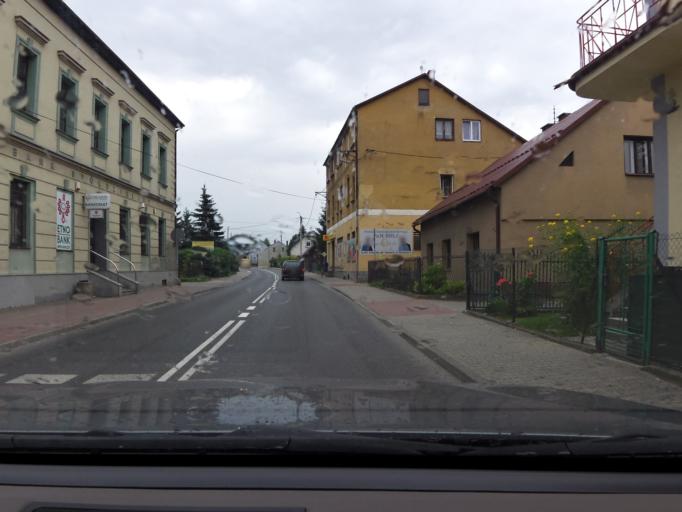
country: PL
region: Silesian Voivodeship
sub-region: Powiat zywiecki
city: Milowka
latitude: 49.5558
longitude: 19.0883
